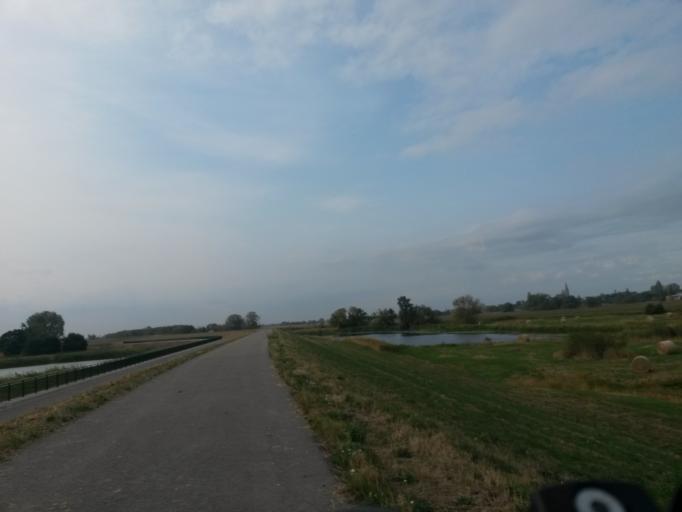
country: DE
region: Saxony-Anhalt
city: Tangermunde
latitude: 52.5563
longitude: 11.9979
